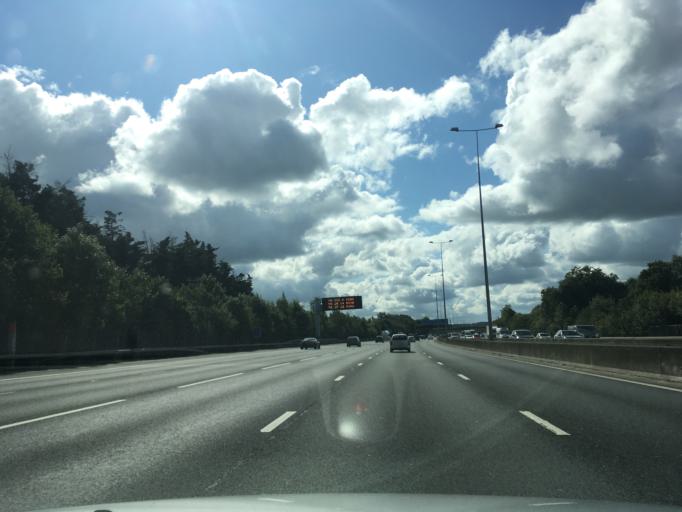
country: GB
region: England
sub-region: Surrey
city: Egham
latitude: 51.4194
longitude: -0.5394
